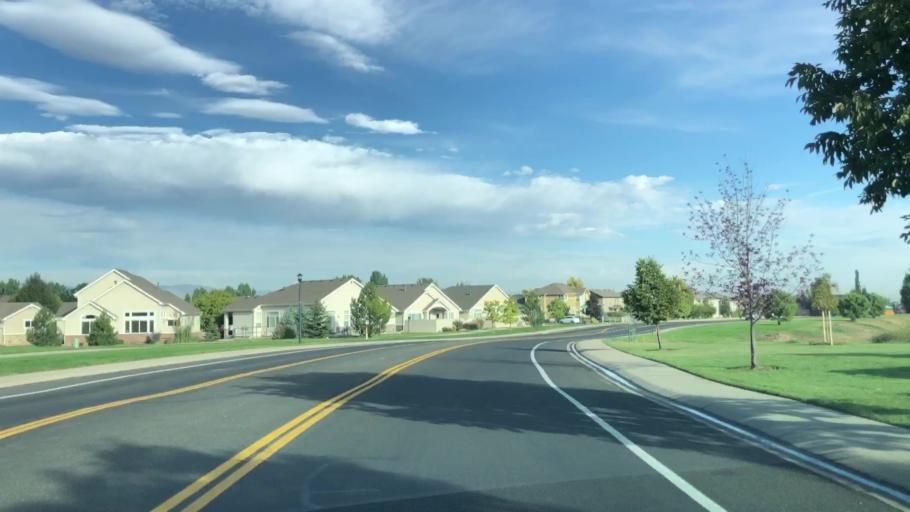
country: US
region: Colorado
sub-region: Weld County
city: Windsor
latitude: 40.4694
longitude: -104.9787
